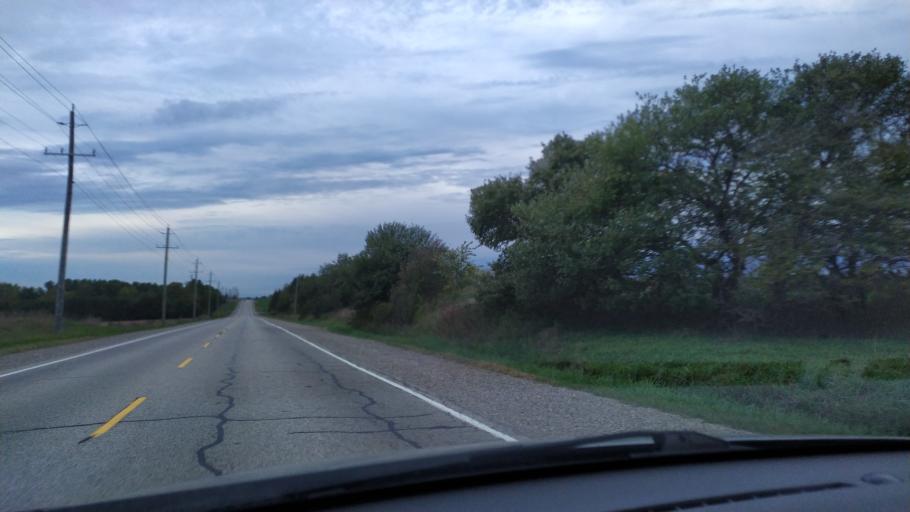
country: CA
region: Ontario
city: Stratford
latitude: 43.4930
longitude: -80.7700
